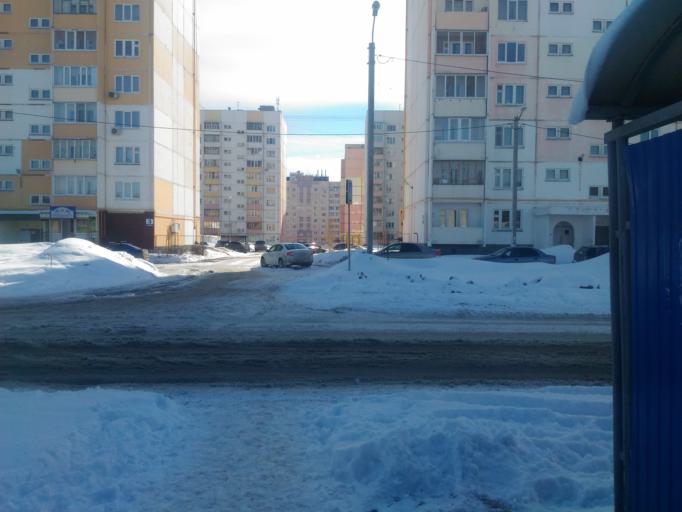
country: RU
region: Ulyanovsk
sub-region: Ulyanovskiy Rayon
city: Ulyanovsk
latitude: 54.3496
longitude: 48.3450
